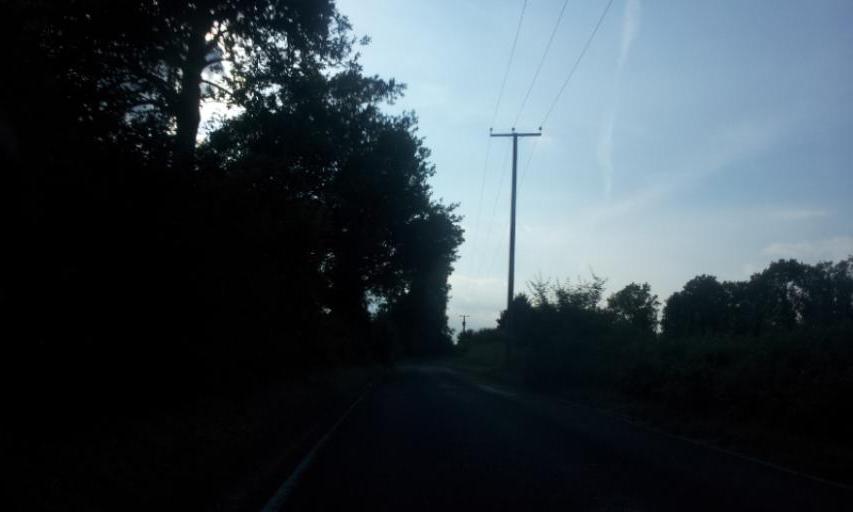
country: GB
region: England
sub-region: Kent
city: Boxley
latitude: 51.2949
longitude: 0.5316
